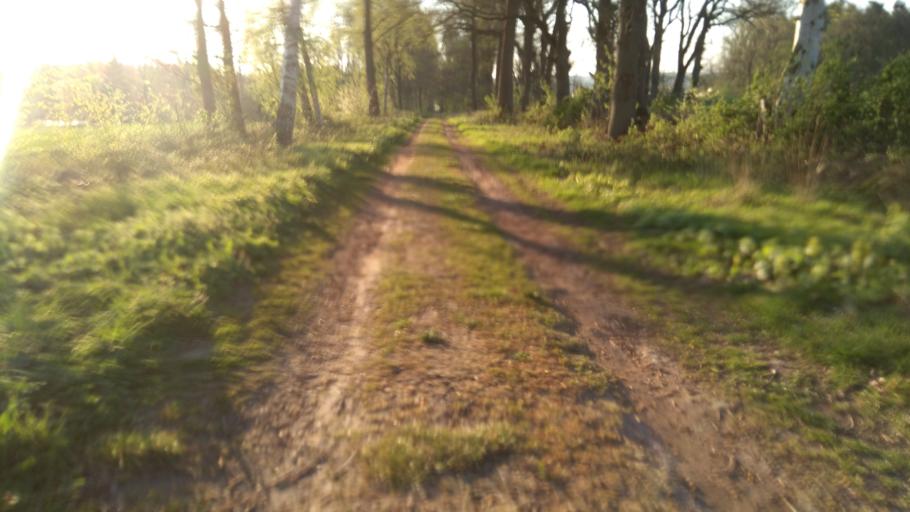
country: DE
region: Lower Saxony
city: Harsefeld
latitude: 53.4684
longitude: 9.5016
